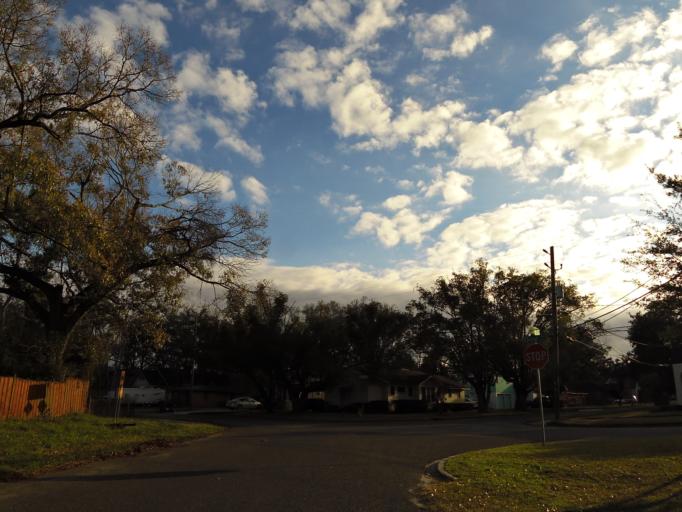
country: US
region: Florida
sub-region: Duval County
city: Jacksonville
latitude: 30.3121
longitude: -81.7095
